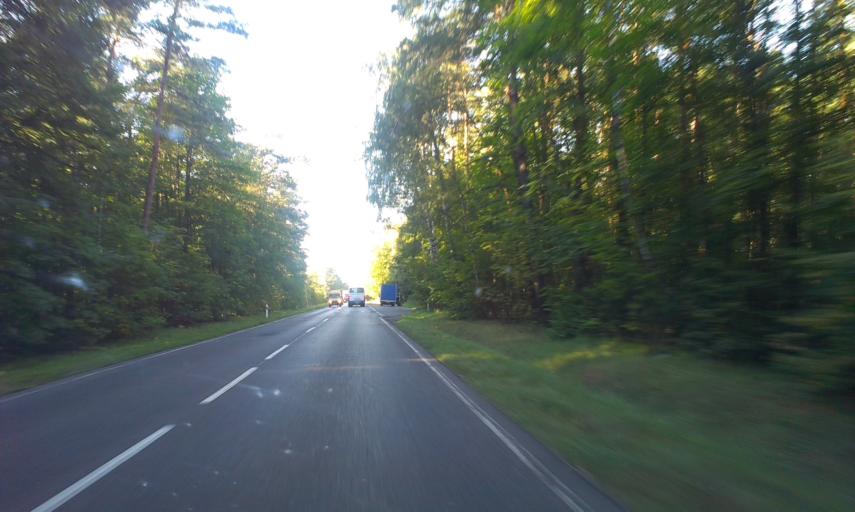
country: PL
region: Kujawsko-Pomorskie
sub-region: Powiat tucholski
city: Cekcyn
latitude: 53.5220
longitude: 17.9508
